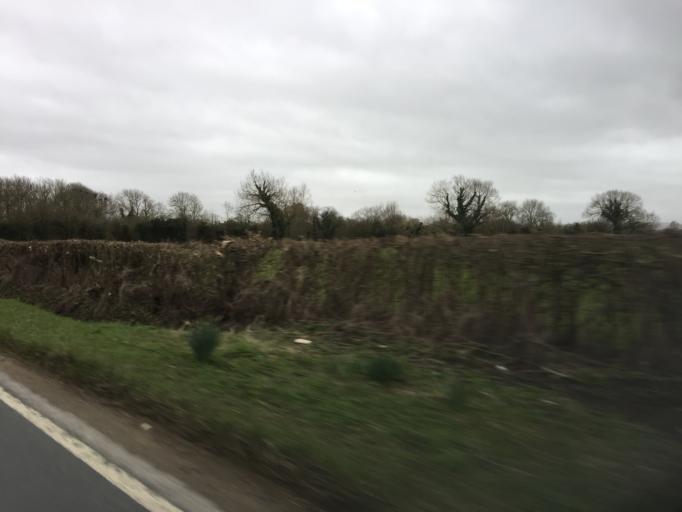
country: GB
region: England
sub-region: Oxfordshire
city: Stanford in the Vale
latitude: 51.6332
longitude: -1.5077
